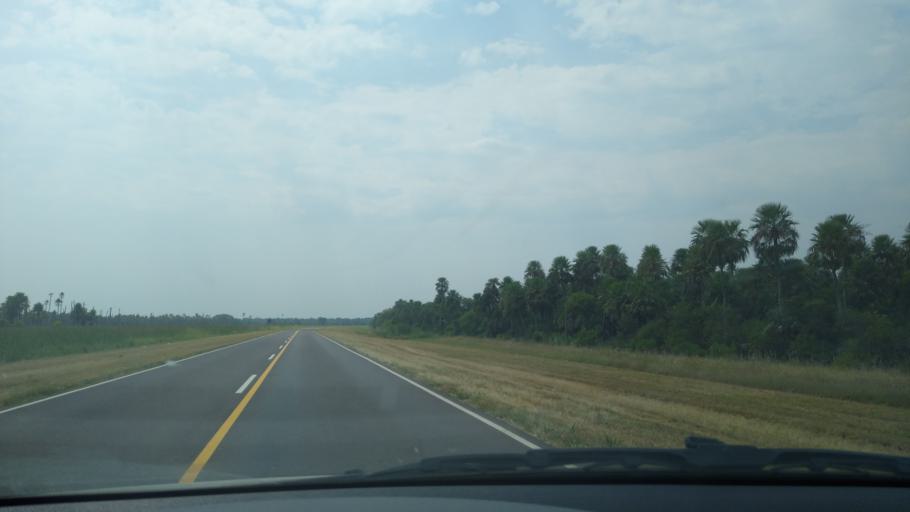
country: AR
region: Chaco
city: Margarita Belen
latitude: -27.0753
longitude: -58.9618
